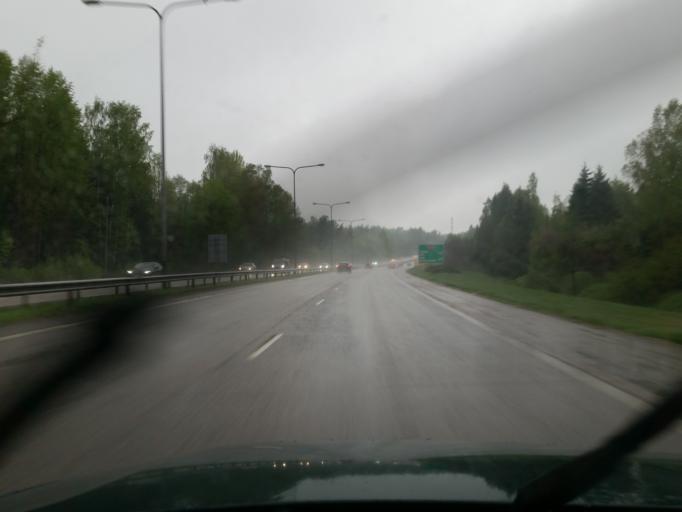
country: FI
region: Uusimaa
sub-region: Helsinki
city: Kauniainen
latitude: 60.2013
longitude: 24.7292
